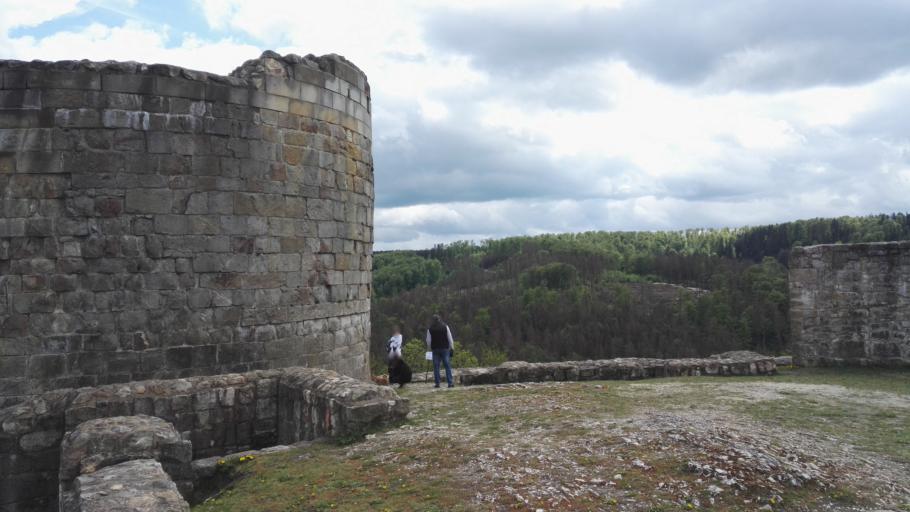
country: DE
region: North Rhine-Westphalia
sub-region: Regierungsbezirk Detmold
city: Detmold
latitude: 51.8760
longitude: 8.8799
